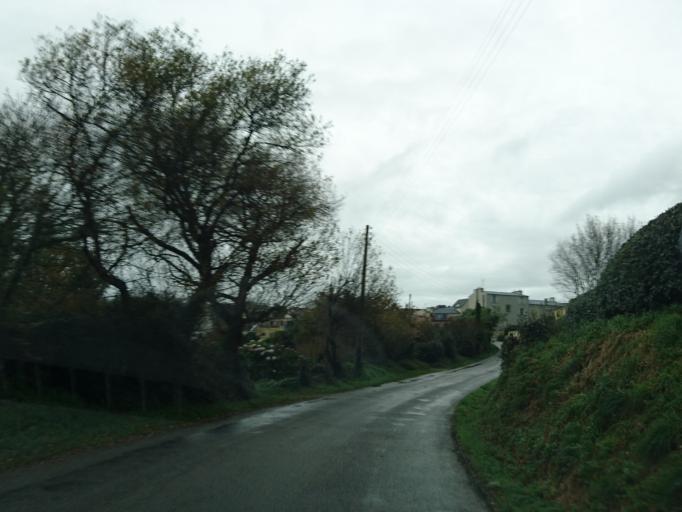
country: FR
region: Brittany
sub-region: Departement du Finistere
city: Plougonvelin
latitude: 48.3592
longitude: -4.6771
